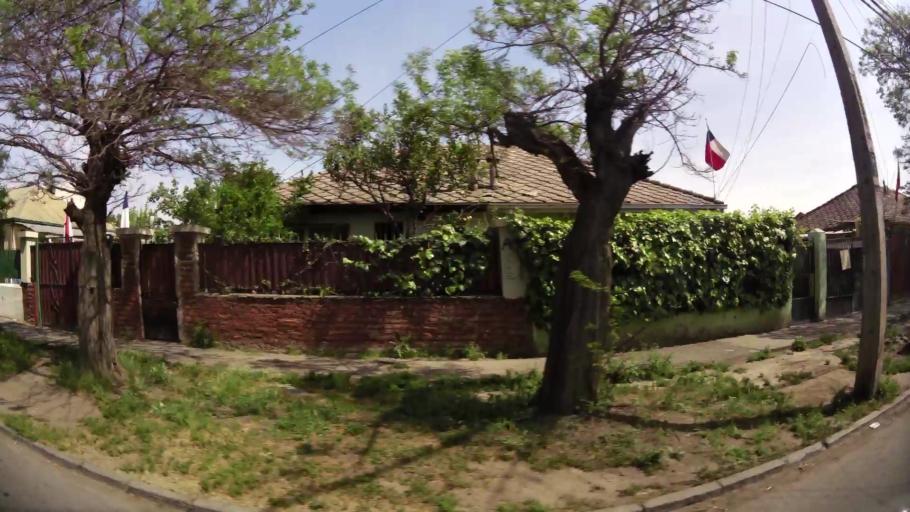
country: CL
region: Santiago Metropolitan
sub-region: Provincia de Santiago
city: Lo Prado
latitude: -33.4200
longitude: -70.6979
